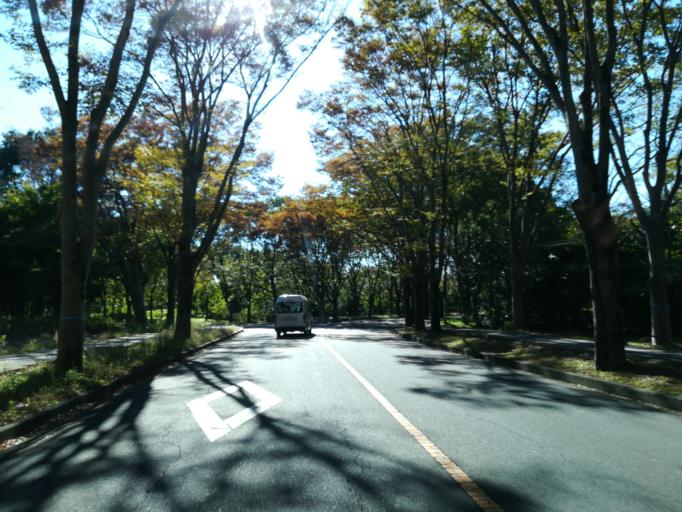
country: JP
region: Ibaraki
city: Naka
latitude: 36.1001
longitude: 140.1056
